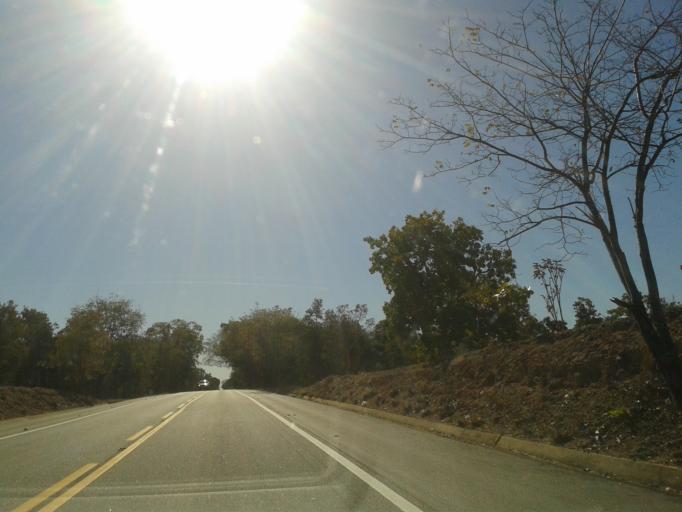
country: BR
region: Goias
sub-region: Itapuranga
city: Itapuranga
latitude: -15.4721
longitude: -50.3437
